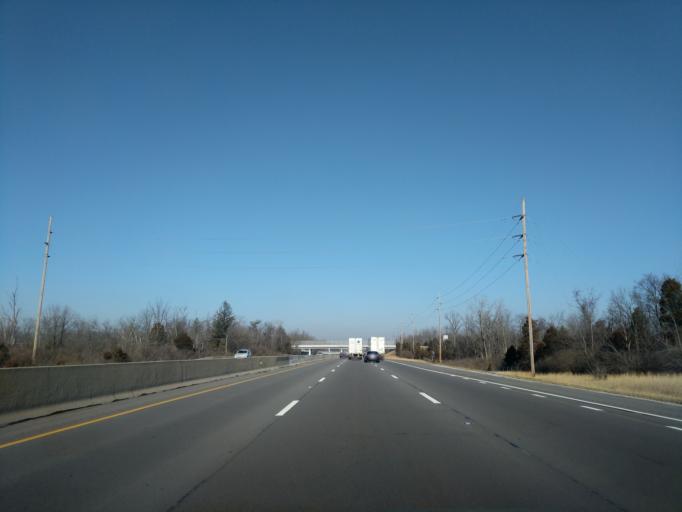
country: US
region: Ohio
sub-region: Montgomery County
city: Vandalia
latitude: 39.9079
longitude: -84.1881
